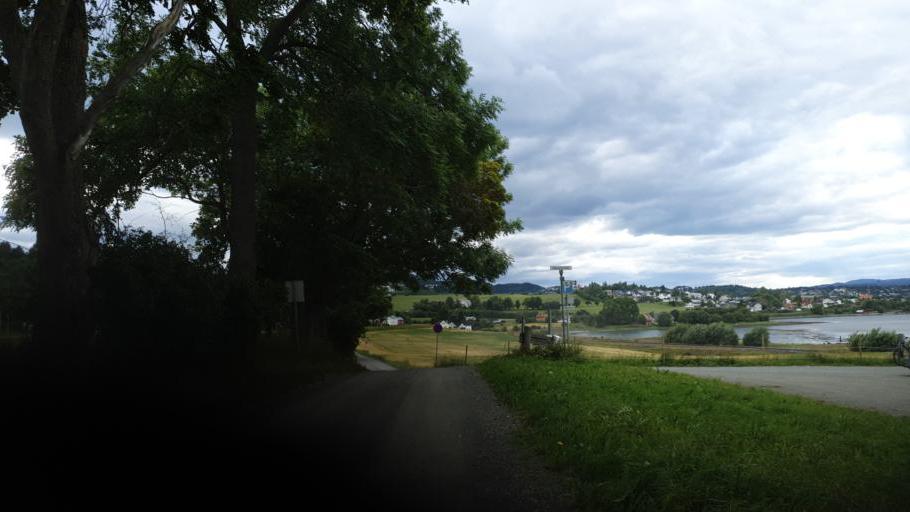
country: NO
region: Sor-Trondelag
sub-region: Malvik
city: Malvik
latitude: 63.4323
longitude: 10.5675
